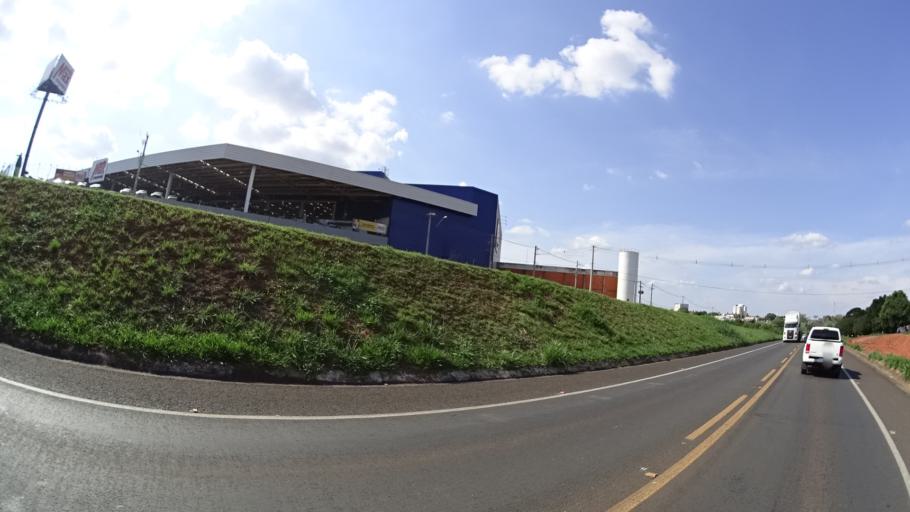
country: BR
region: Sao Paulo
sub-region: Sao Jose Do Rio Preto
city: Sao Jose do Rio Preto
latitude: -20.8406
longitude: -49.3696
